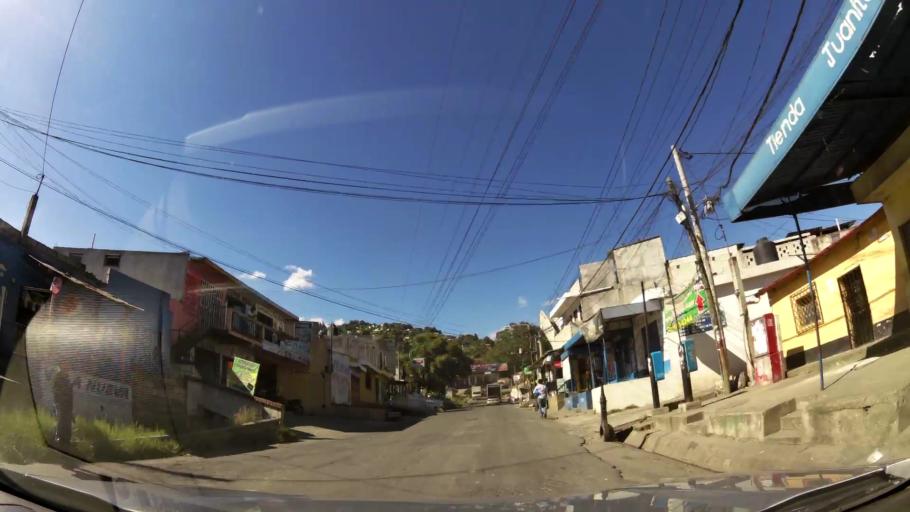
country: GT
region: Guatemala
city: Villa Nueva
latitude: 14.5468
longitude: -90.6185
